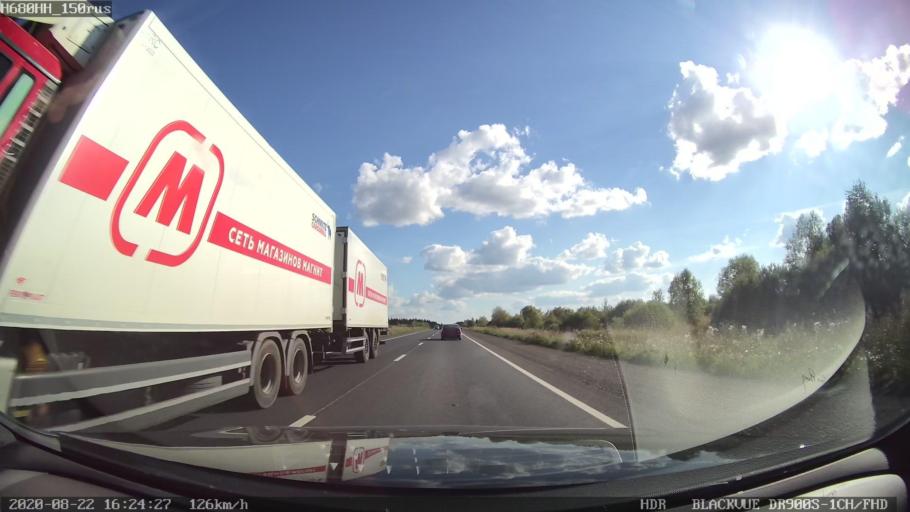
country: RU
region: Tverskaya
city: Rameshki
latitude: 57.3368
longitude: 36.0951
